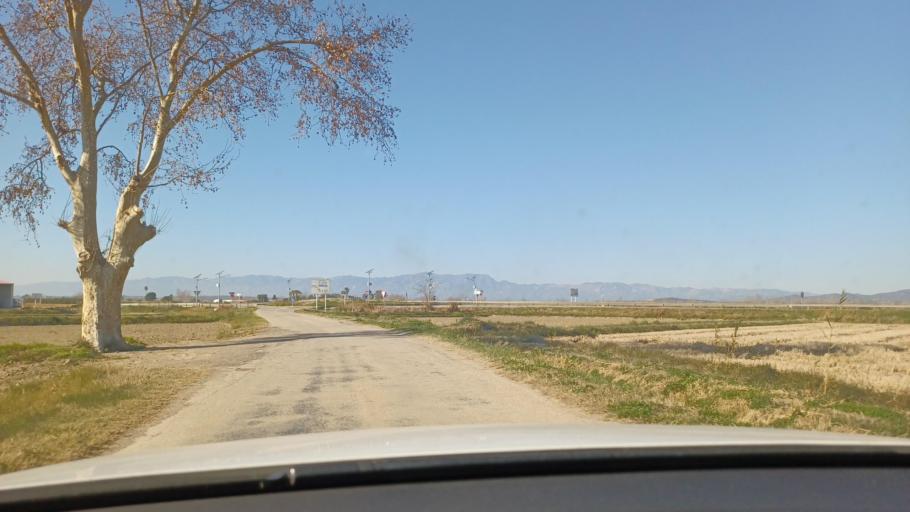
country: ES
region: Catalonia
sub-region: Provincia de Tarragona
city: Amposta
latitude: 40.7041
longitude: 0.6339
